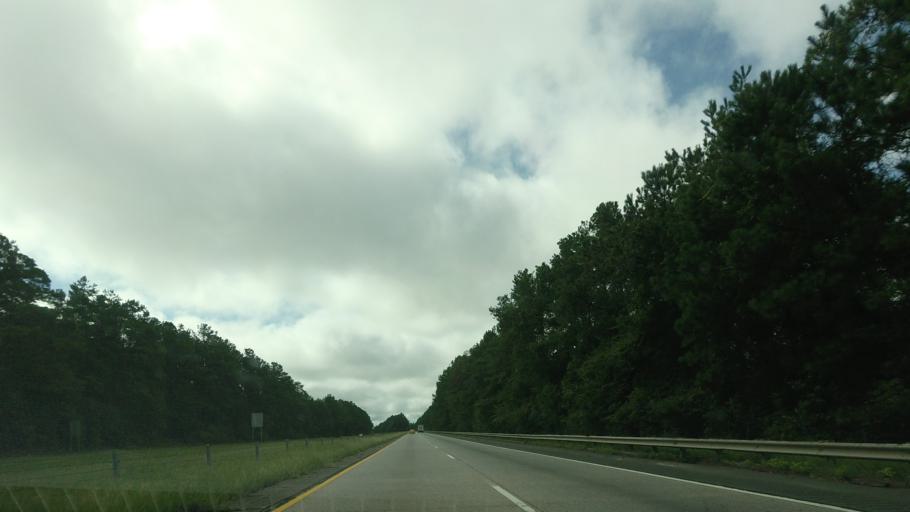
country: US
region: Georgia
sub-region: Bibb County
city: Macon
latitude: 32.7709
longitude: -83.5576
